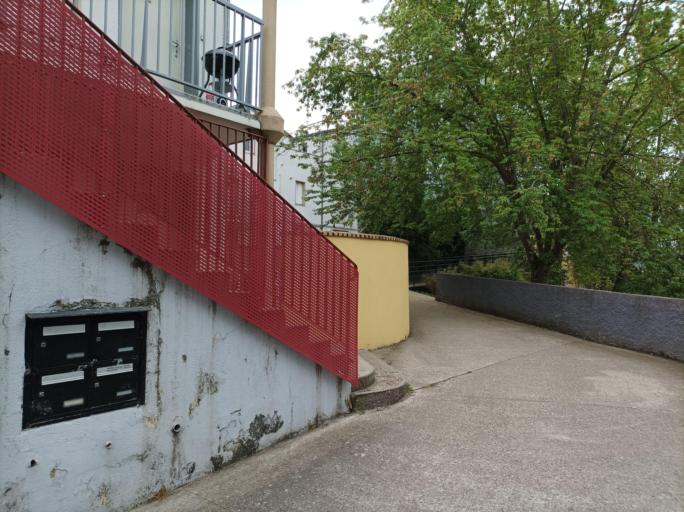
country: FR
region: Haute-Normandie
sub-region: Departement de l'Eure
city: Val-de-Reuil
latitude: 49.2742
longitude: 1.2142
